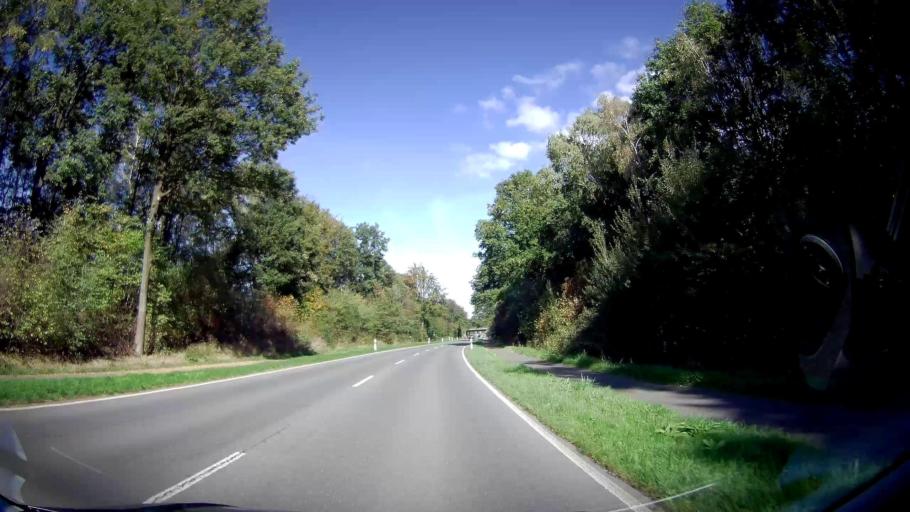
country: DE
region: North Rhine-Westphalia
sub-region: Regierungsbezirk Dusseldorf
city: Hunxe
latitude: 51.6218
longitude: 6.7551
